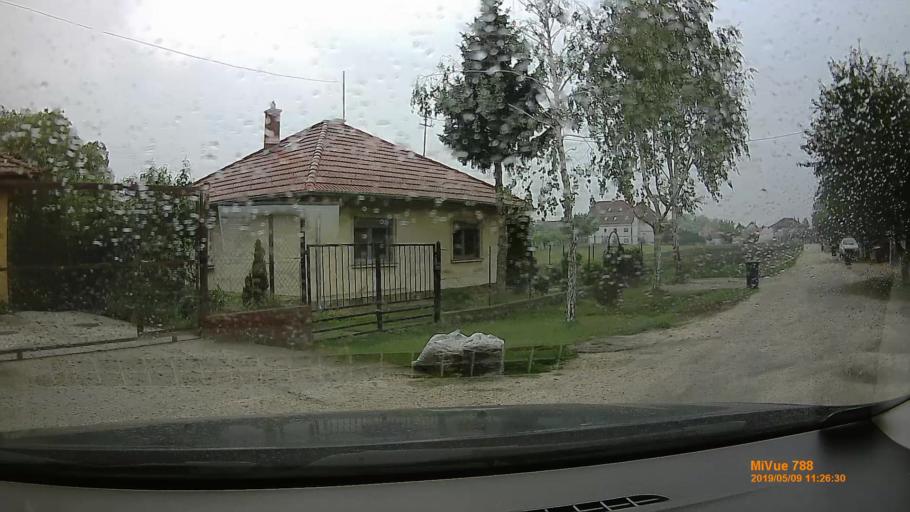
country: HU
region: Budapest
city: Budapest XVI. keruelet
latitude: 47.5337
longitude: 19.1809
